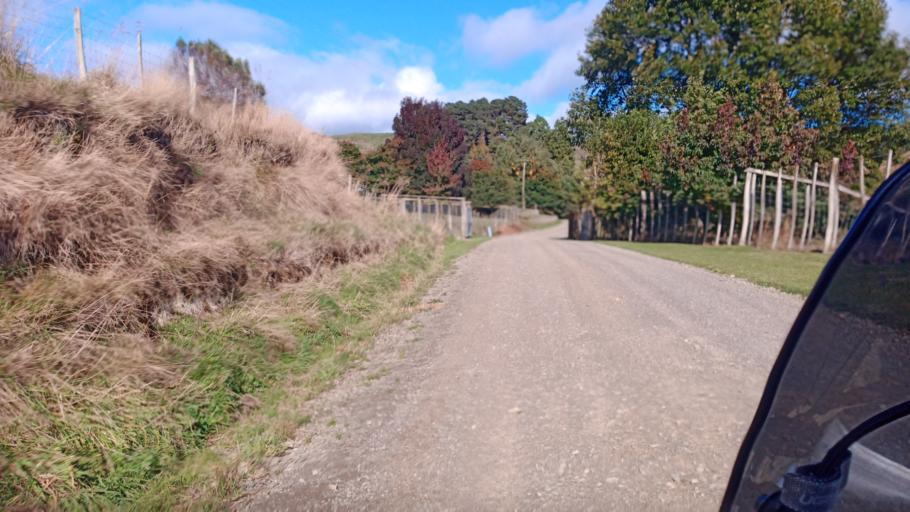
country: NZ
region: Bay of Plenty
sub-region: Opotiki District
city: Opotiki
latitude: -38.4612
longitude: 177.3845
